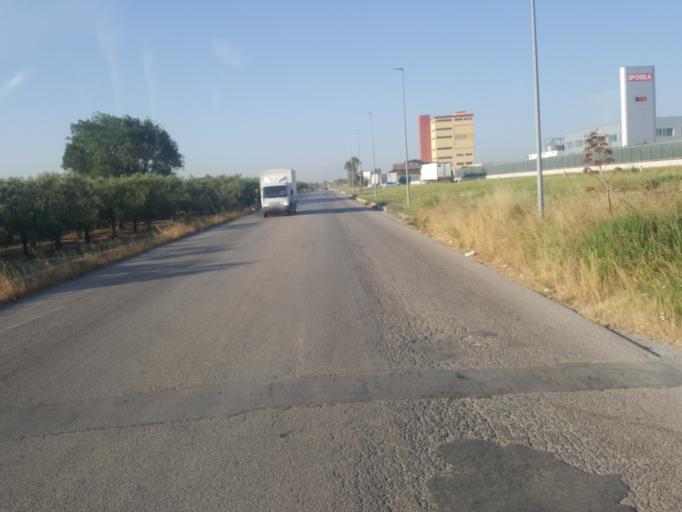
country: IT
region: Apulia
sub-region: Provincia di Foggia
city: Cerignola
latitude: 41.3026
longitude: 15.8982
